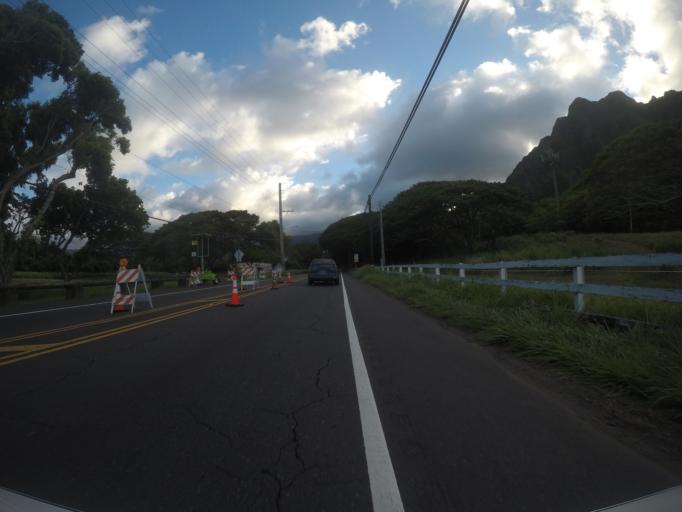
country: US
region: Hawaii
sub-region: Honolulu County
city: Ka'a'awa
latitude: 21.5168
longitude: -157.8387
